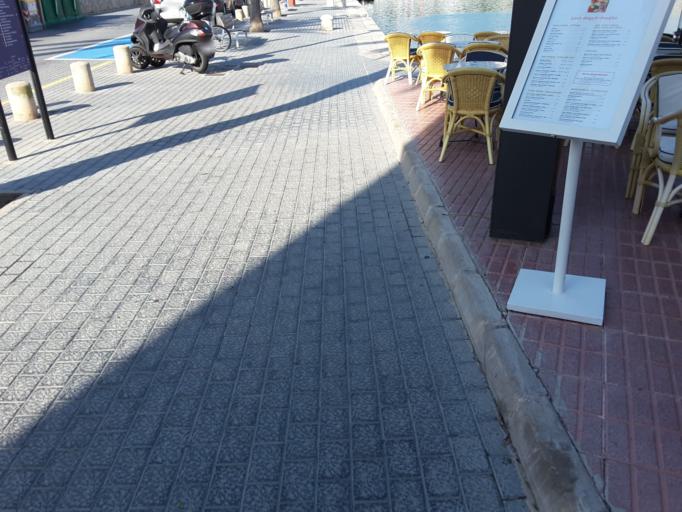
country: ES
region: Balearic Islands
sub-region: Illes Balears
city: Camp de Mar
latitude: 39.5442
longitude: 2.3875
